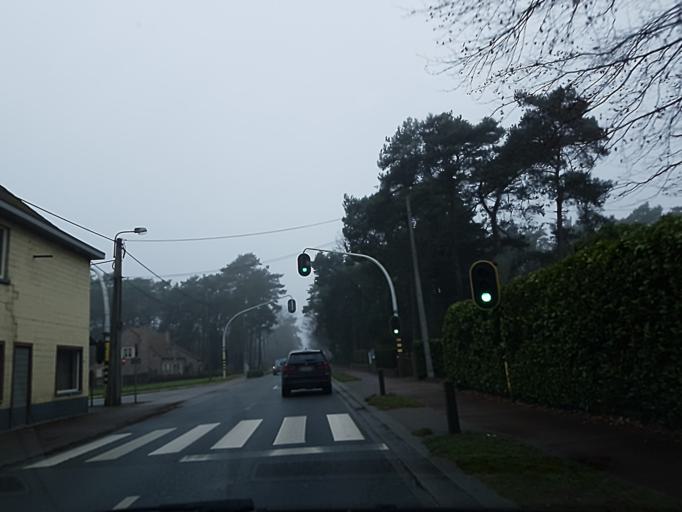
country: BE
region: Flanders
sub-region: Provincie Antwerpen
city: Bonheiden
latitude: 51.0194
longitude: 4.5630
